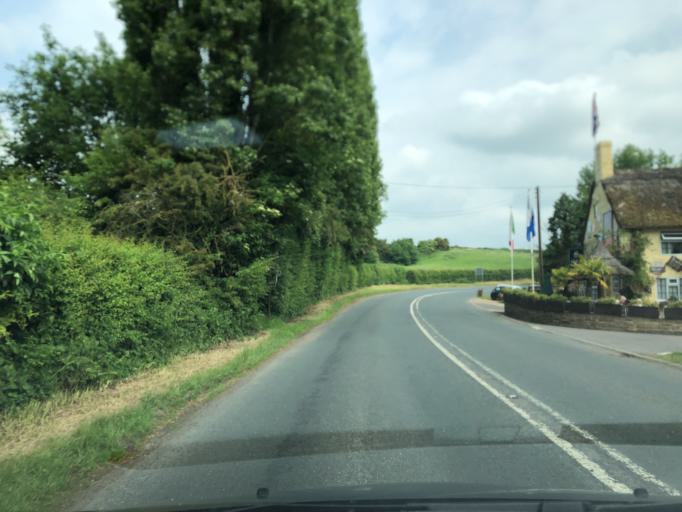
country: GB
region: England
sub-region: North Yorkshire
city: Thirsk
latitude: 54.1707
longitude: -1.3949
